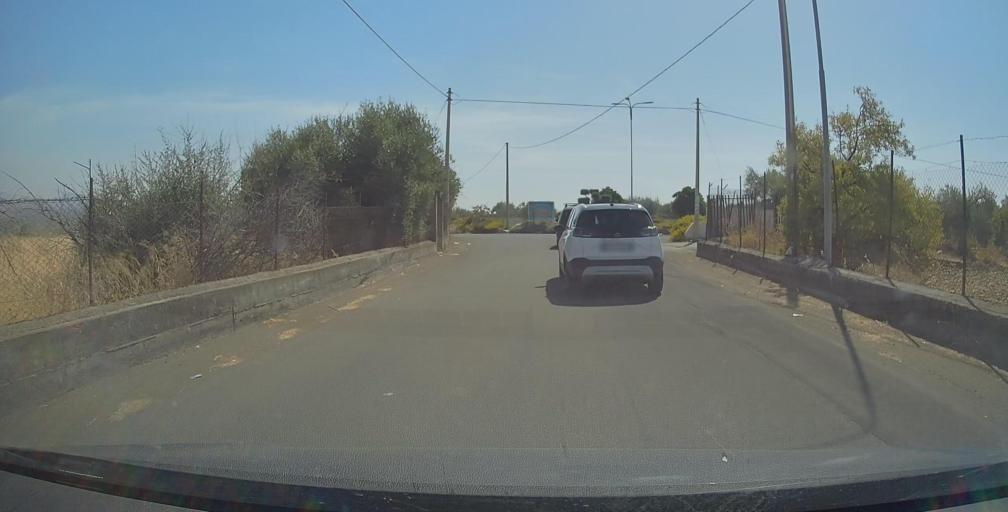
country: IT
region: Sicily
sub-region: Catania
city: Palazzolo
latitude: 37.5415
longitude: 14.9304
